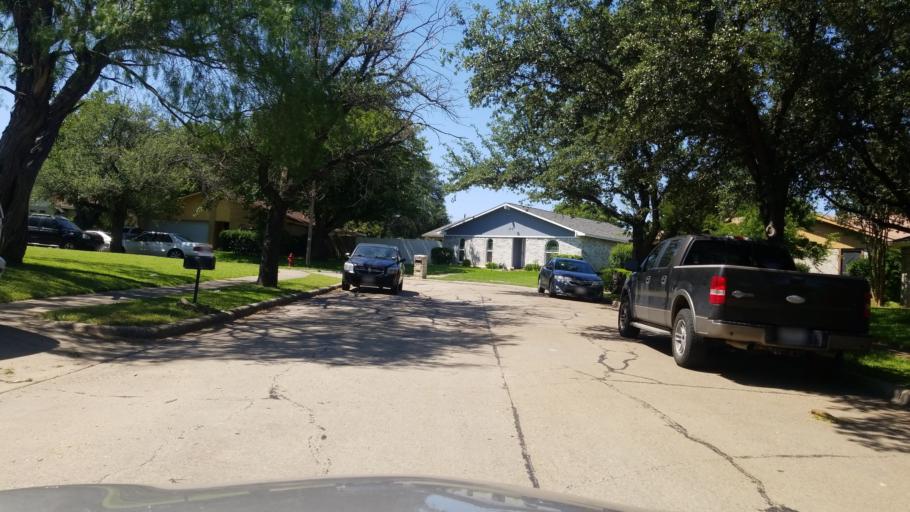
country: US
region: Texas
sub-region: Dallas County
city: Grand Prairie
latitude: 32.6928
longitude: -96.9960
